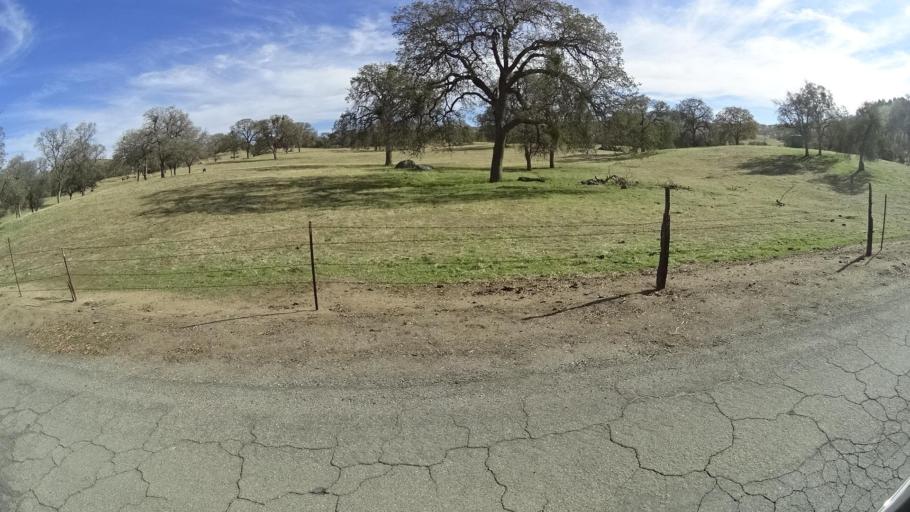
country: US
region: California
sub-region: Kern County
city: Oildale
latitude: 35.5837
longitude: -118.8221
